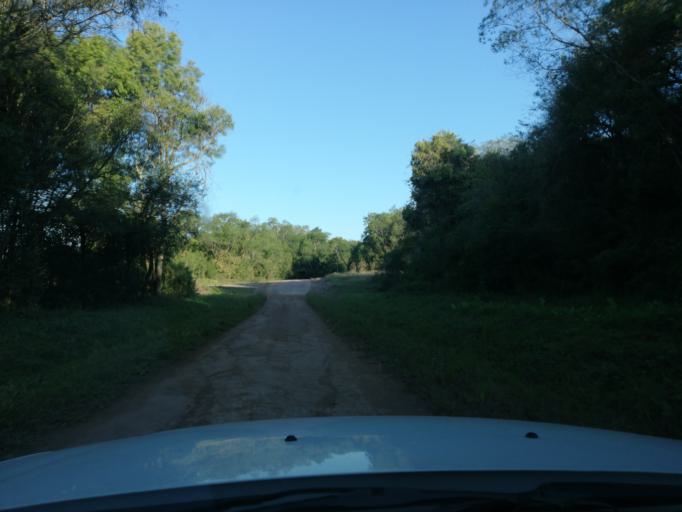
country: AR
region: Misiones
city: Cerro Cora
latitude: -27.6233
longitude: -55.7045
